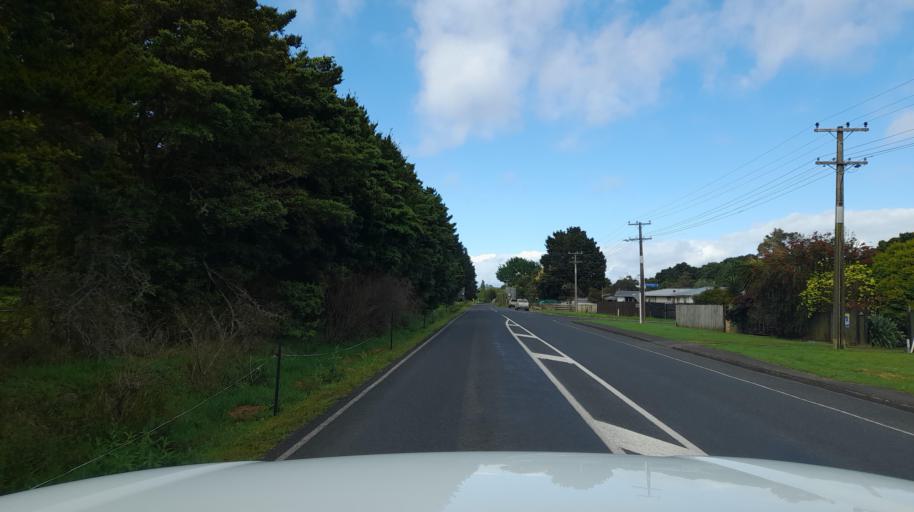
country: NZ
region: Northland
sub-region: Far North District
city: Moerewa
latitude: -35.3949
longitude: 174.0073
